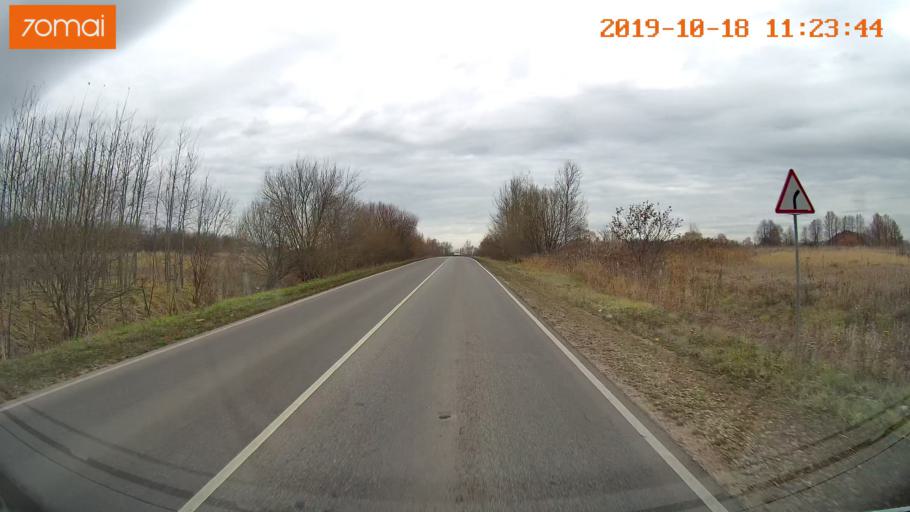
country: RU
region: Tula
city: Kimovsk
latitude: 54.1057
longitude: 38.5947
